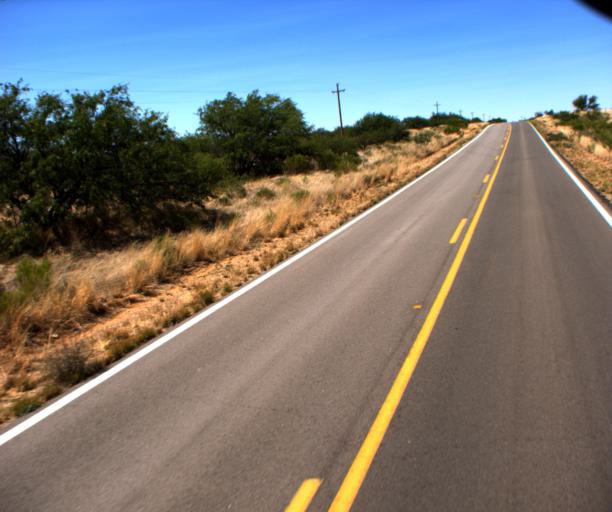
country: US
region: Arizona
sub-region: Santa Cruz County
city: Tubac
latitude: 31.5027
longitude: -111.5459
